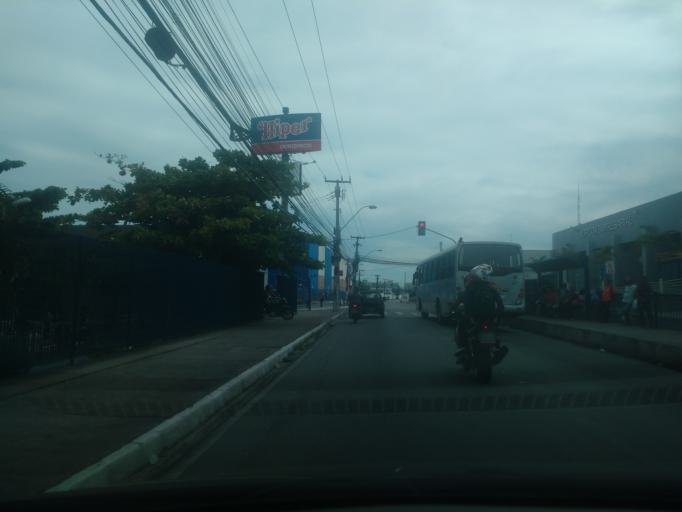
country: BR
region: Alagoas
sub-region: Maceio
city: Maceio
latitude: -9.6488
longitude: -35.7171
